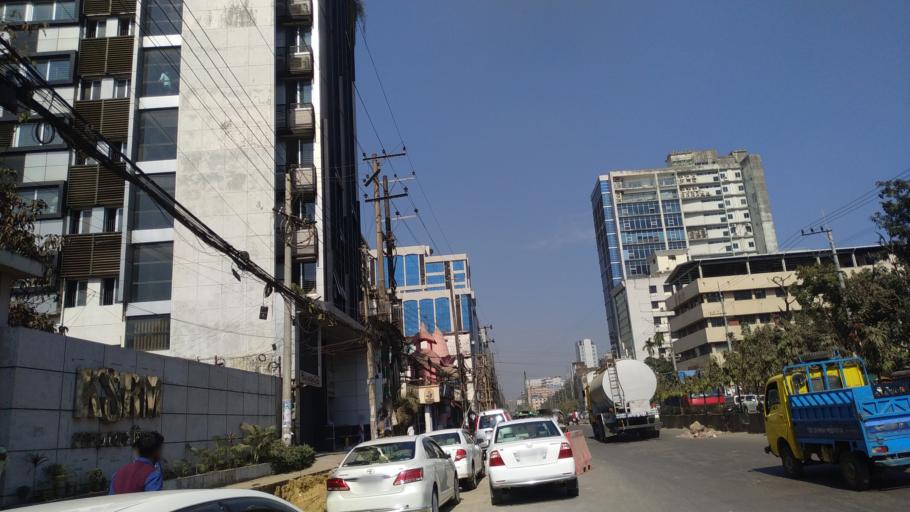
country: BD
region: Chittagong
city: Chittagong
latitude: 22.3202
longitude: 91.8120
